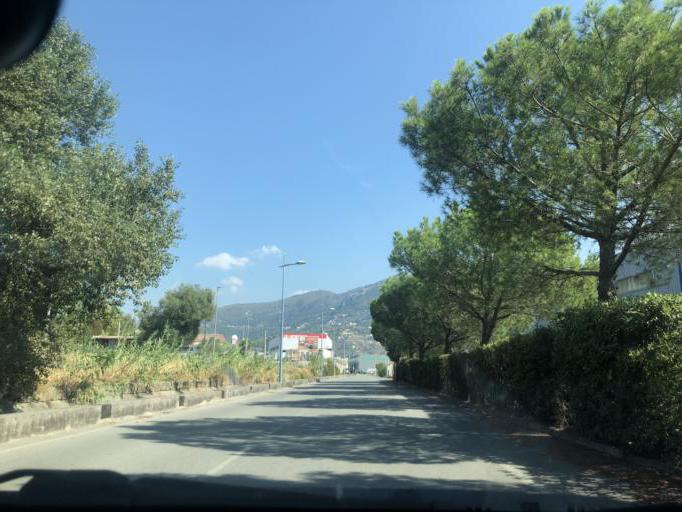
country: FR
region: Provence-Alpes-Cote d'Azur
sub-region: Departement des Alpes-Maritimes
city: Colomars
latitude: 43.7729
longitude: 7.2059
